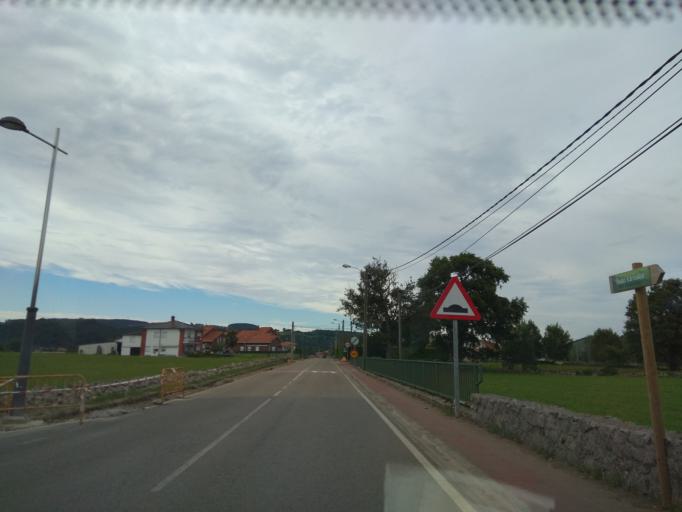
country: ES
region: Cantabria
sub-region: Provincia de Cantabria
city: Solorzano
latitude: 43.3860
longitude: -3.5883
